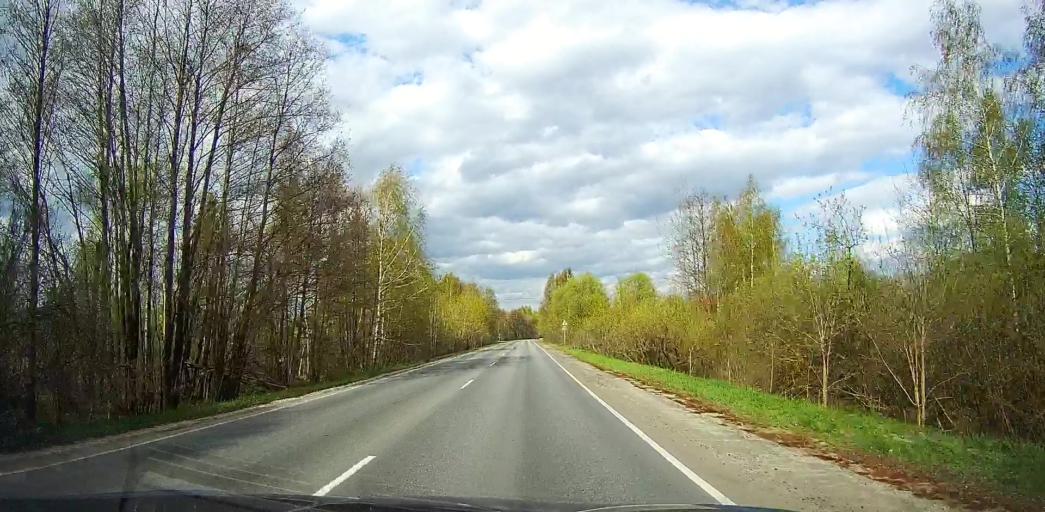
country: RU
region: Moskovskaya
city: Rakhmanovo
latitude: 55.7324
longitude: 38.6325
